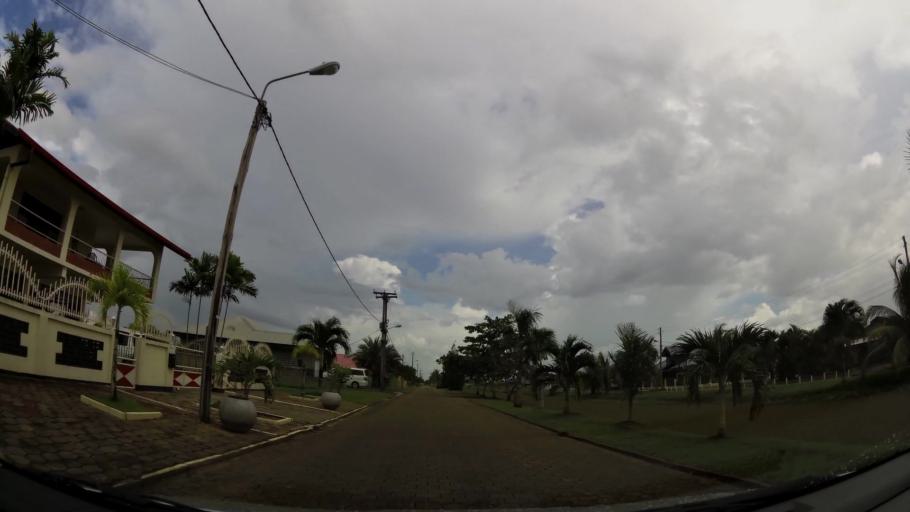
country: SR
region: Commewijne
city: Nieuw Amsterdam
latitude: 5.8630
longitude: -55.1220
